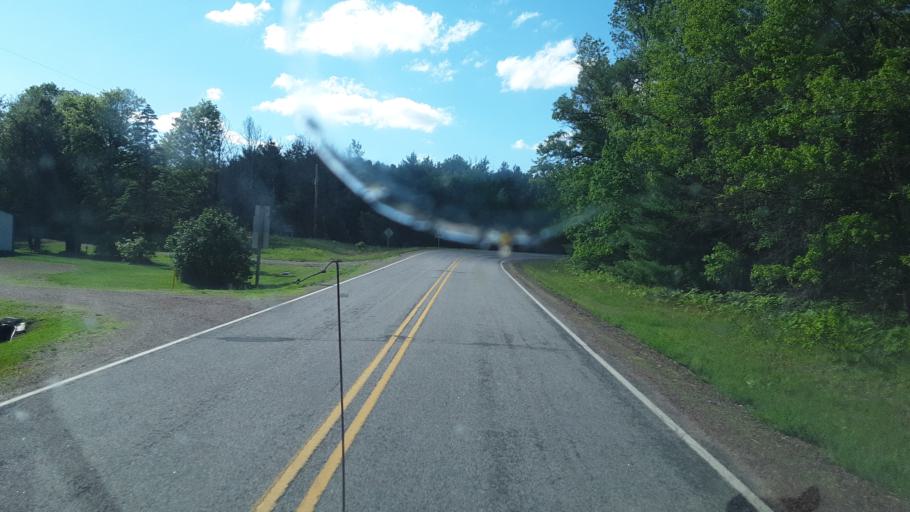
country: US
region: Wisconsin
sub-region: Wood County
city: Nekoosa
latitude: 44.3012
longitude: -90.1255
